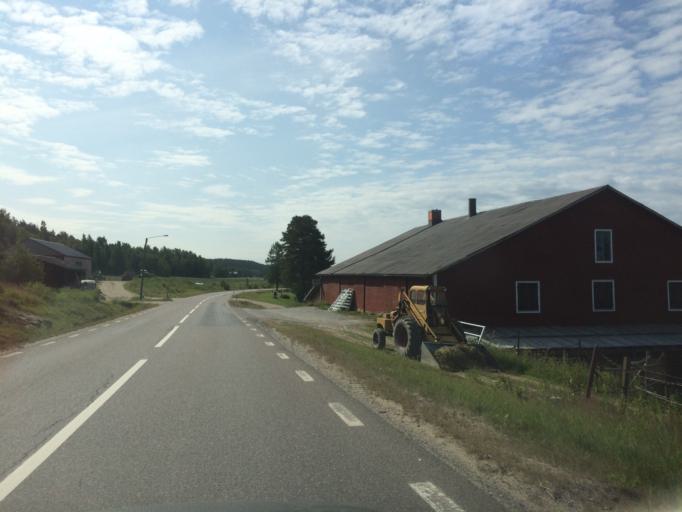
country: SE
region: Vaesternorrland
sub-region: Kramfors Kommun
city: Bollstabruk
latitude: 63.0841
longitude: 17.7743
